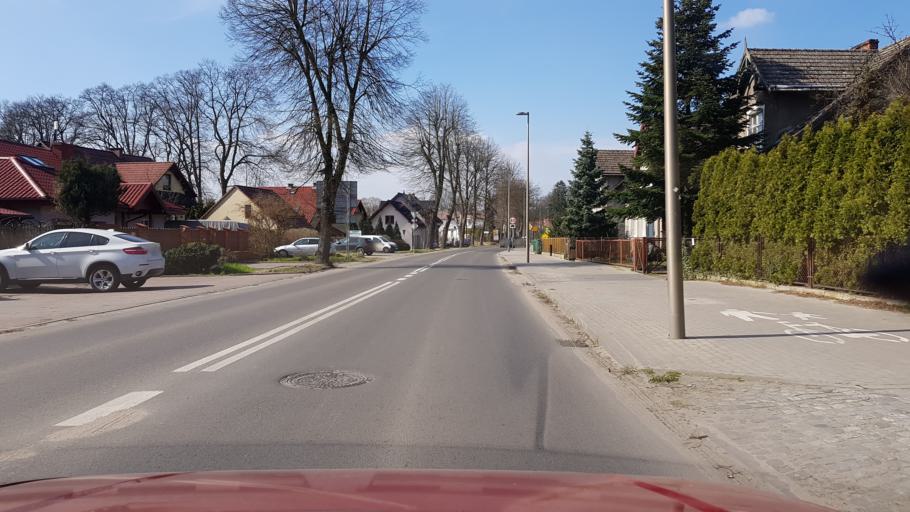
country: PL
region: West Pomeranian Voivodeship
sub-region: Powiat goleniowski
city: Goleniow
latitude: 53.5678
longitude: 14.8222
